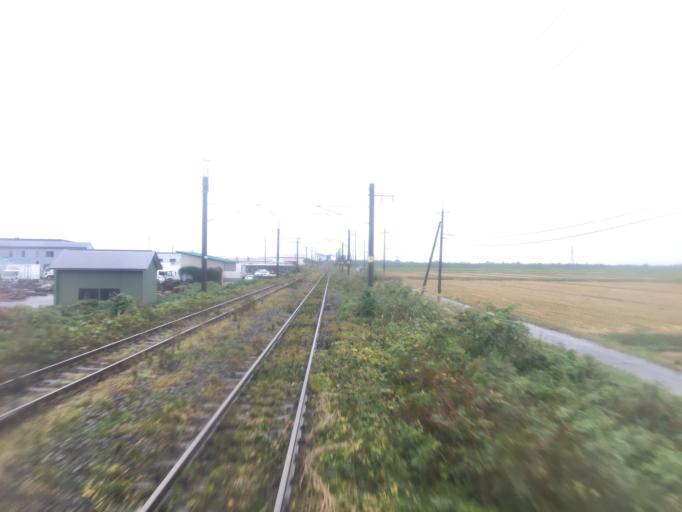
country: JP
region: Yamagata
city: Sakata
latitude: 38.8875
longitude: 139.9097
